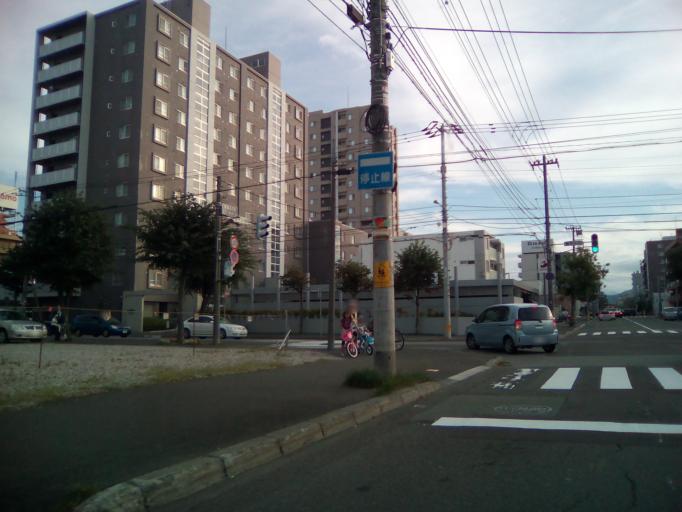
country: JP
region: Hokkaido
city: Sapporo
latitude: 43.0481
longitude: 141.3797
